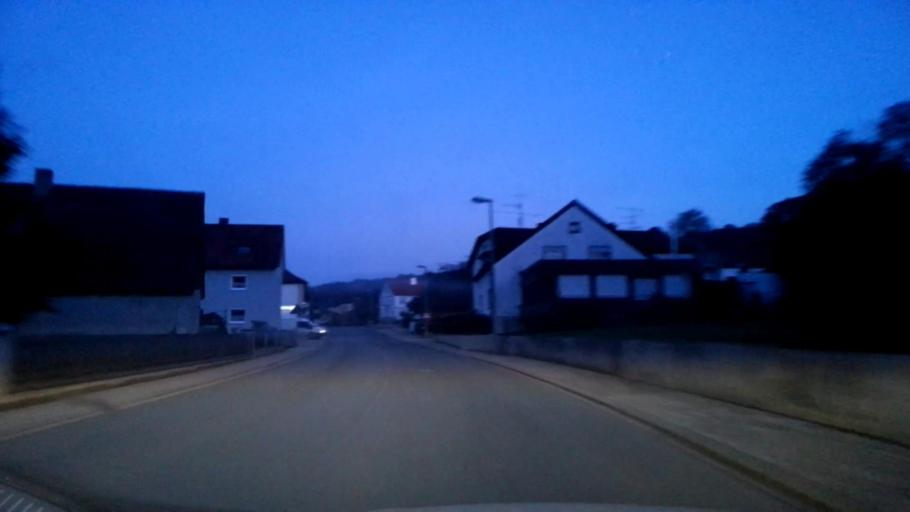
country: DE
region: Bavaria
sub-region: Upper Franconia
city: Pettstadt
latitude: 49.8467
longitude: 10.8942
